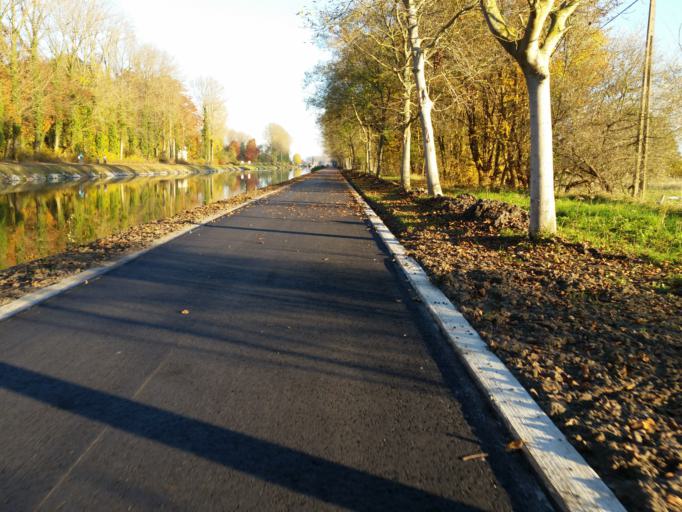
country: BE
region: Flanders
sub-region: Provincie Vlaams-Brabant
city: Haacht
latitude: 50.9498
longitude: 4.6283
